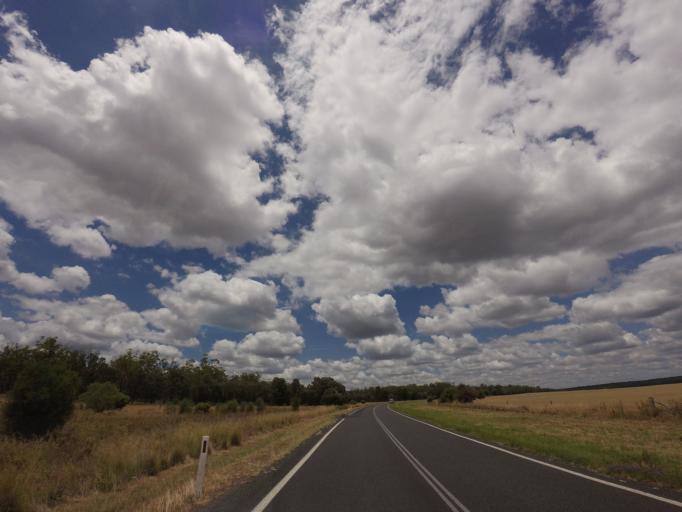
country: AU
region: Queensland
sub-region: Goondiwindi
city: Goondiwindi
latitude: -28.0013
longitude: 150.8980
